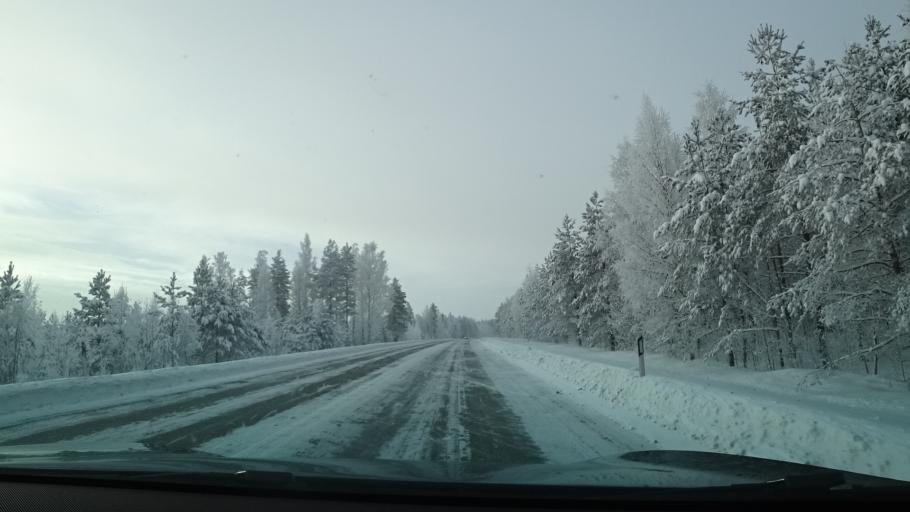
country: FI
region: South Karelia
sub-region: Imatra
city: Saari
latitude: 61.7888
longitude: 29.7229
